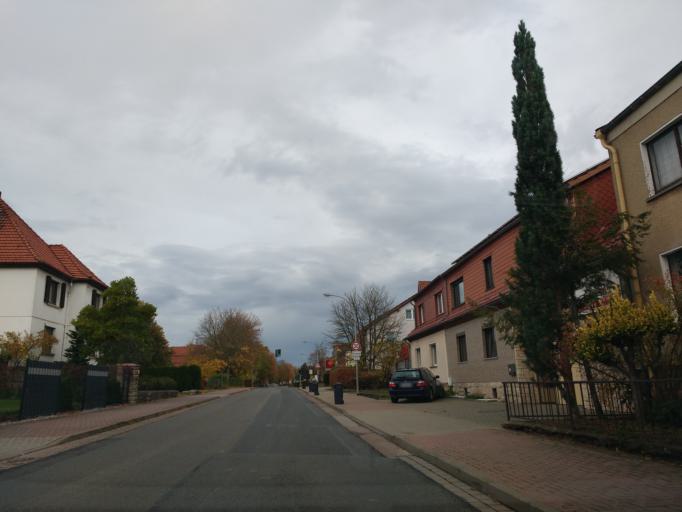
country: DE
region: Thuringia
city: Niederorschel
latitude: 51.3755
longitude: 10.4218
